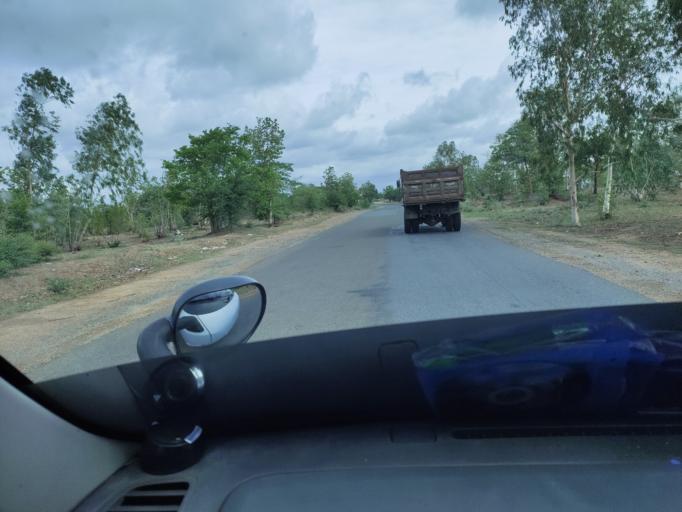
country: MM
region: Magway
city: Chauk
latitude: 20.9792
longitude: 95.0496
